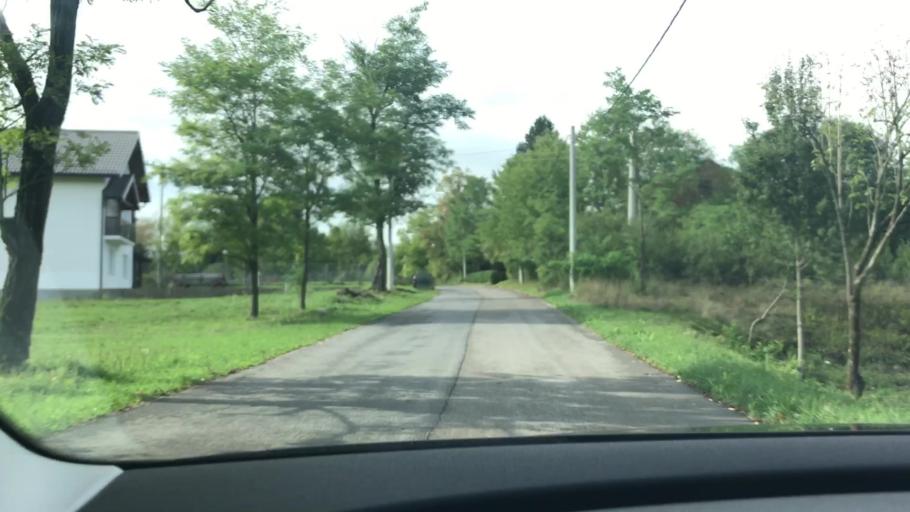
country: BA
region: Federation of Bosnia and Herzegovina
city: Izacic
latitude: 44.8766
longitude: 15.7152
